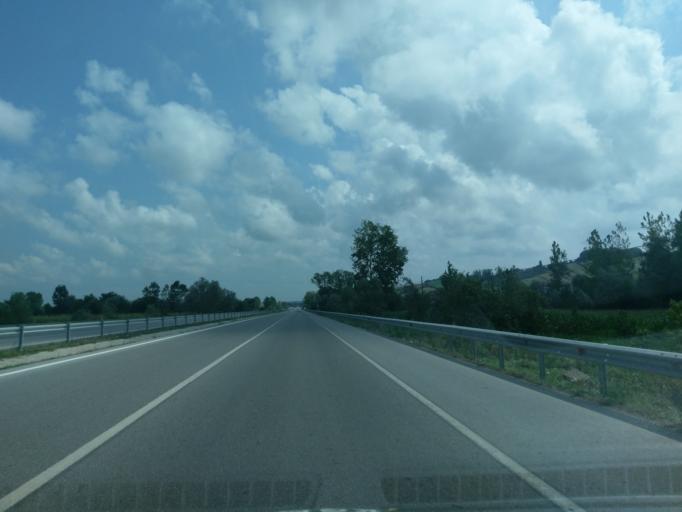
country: TR
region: Samsun
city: Alacam
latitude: 41.6109
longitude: 35.7169
